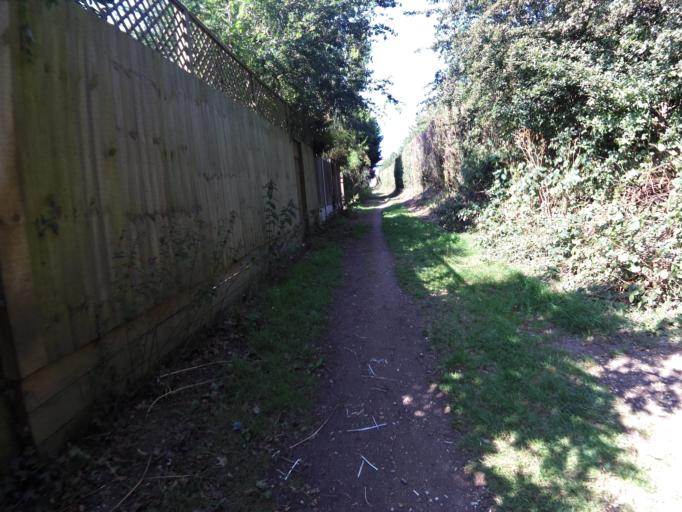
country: GB
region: England
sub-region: Essex
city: West Bergholt
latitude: 51.8858
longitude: 0.8476
